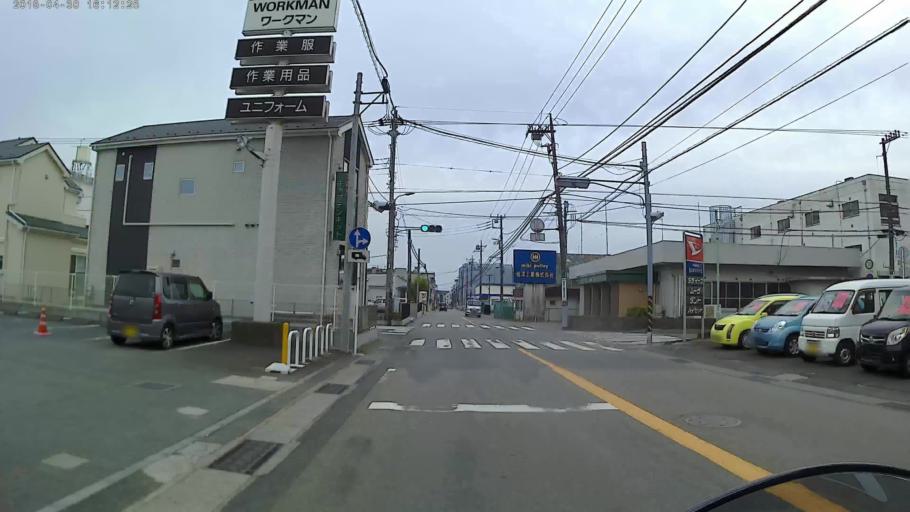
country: JP
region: Kanagawa
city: Minami-rinkan
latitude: 35.4962
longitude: 139.4292
